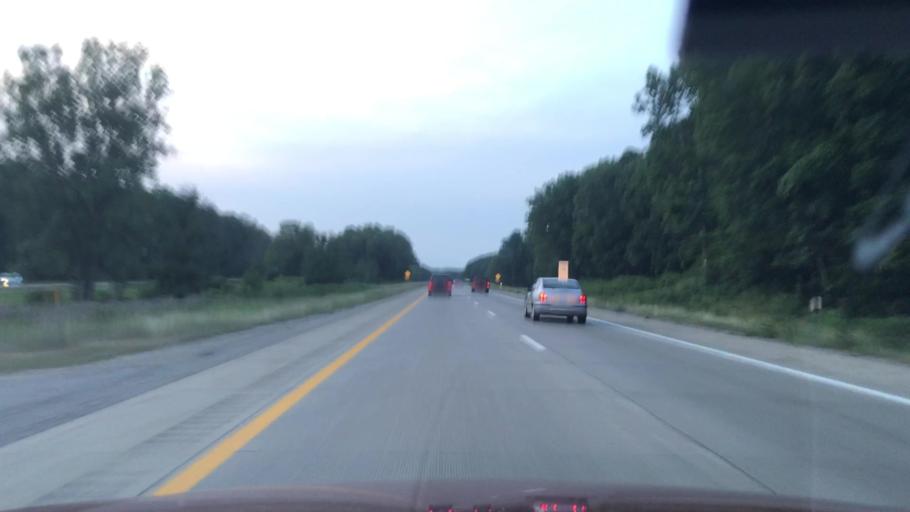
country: US
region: Michigan
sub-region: Kent County
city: Comstock Park
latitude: 43.0540
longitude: -85.6627
